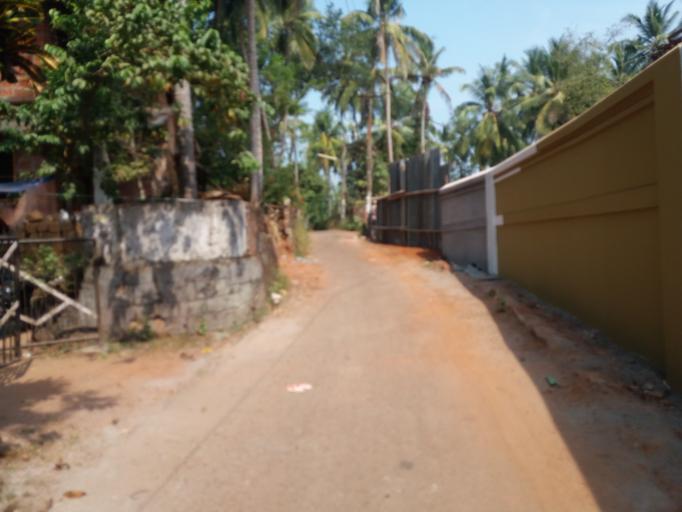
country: IN
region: Kerala
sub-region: Kozhikode
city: Kunnamangalam
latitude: 11.2981
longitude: 75.8191
